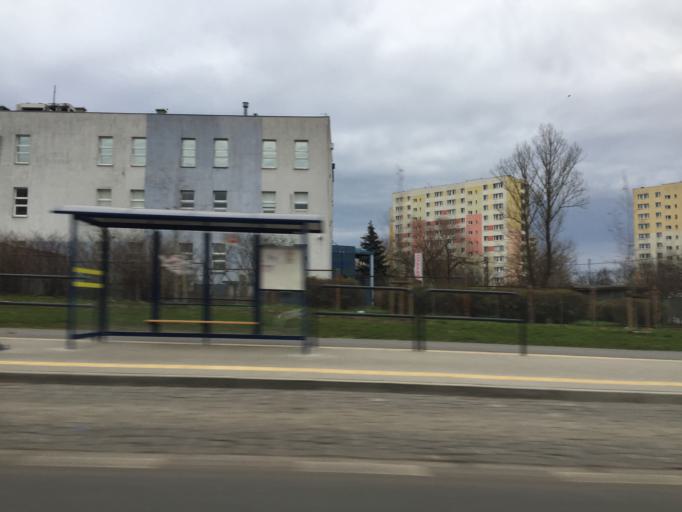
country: PL
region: Kujawsko-Pomorskie
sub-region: Bydgoszcz
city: Bydgoszcz
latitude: 53.1122
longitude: 18.0164
